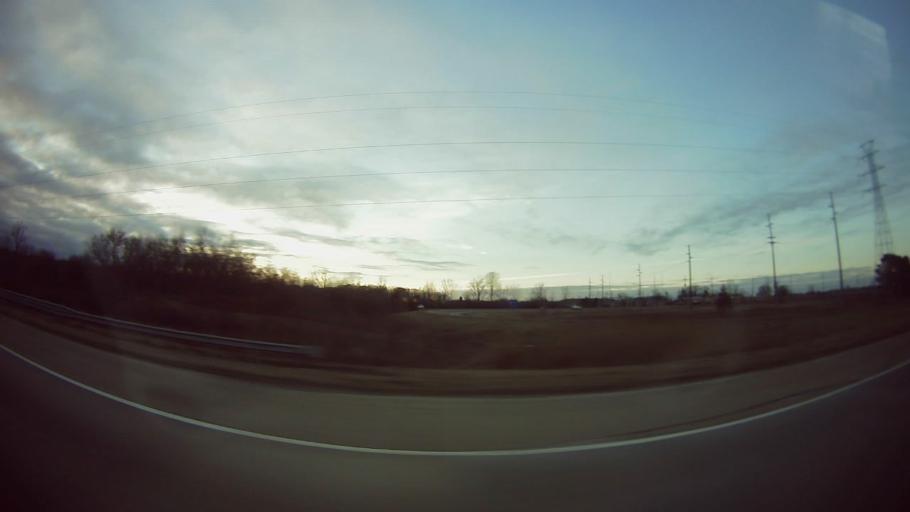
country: US
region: Michigan
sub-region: Monroe County
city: Woodland Beach
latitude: 42.0036
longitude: -83.3161
